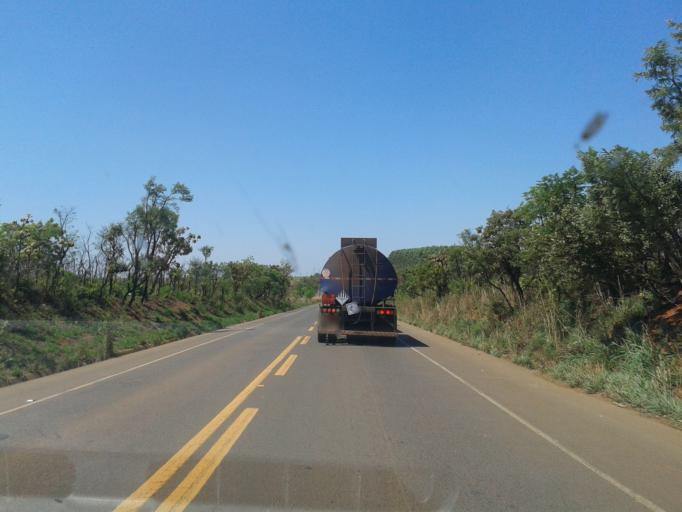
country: BR
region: Minas Gerais
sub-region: Araxa
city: Araxa
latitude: -19.3258
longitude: -47.3816
